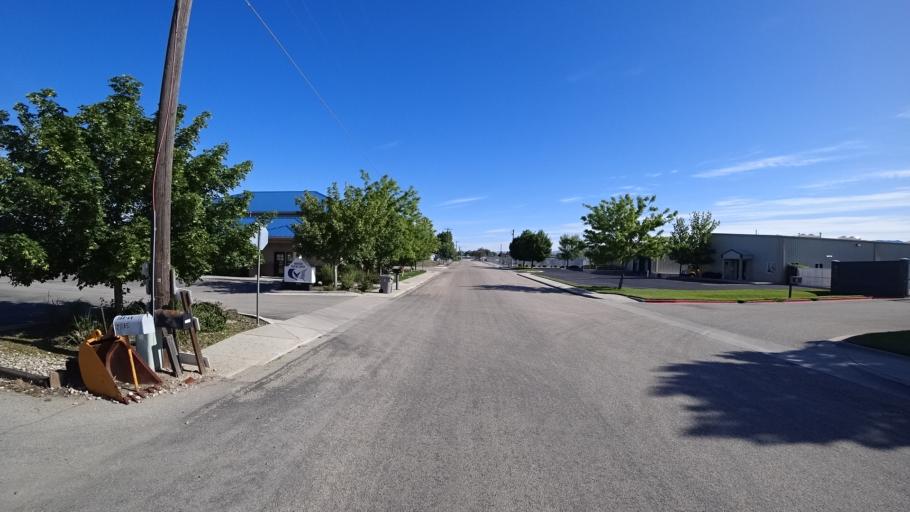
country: US
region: Idaho
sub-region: Ada County
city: Garden City
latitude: 43.5775
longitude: -116.2611
